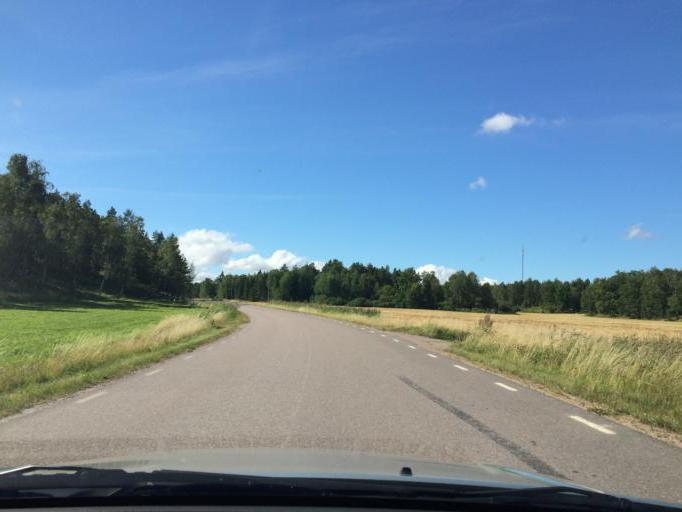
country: SE
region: Soedermanland
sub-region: Eskilstuna Kommun
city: Torshalla
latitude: 59.5230
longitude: 16.4393
